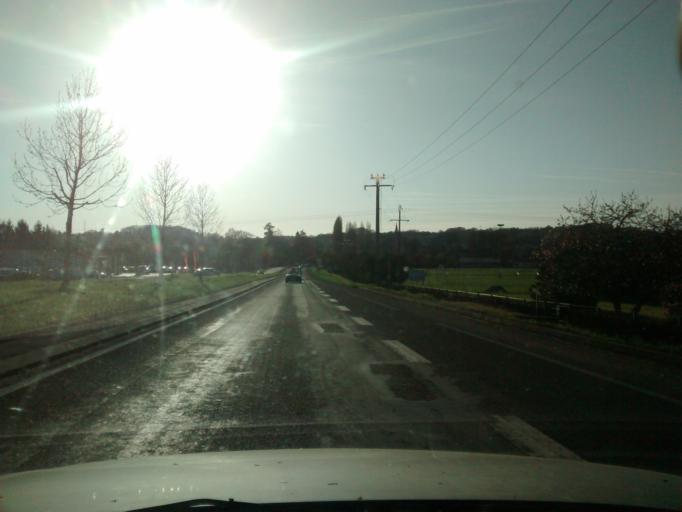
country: FR
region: Pays de la Loire
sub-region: Departement de la Sarthe
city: Change
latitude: 48.0118
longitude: 0.2816
